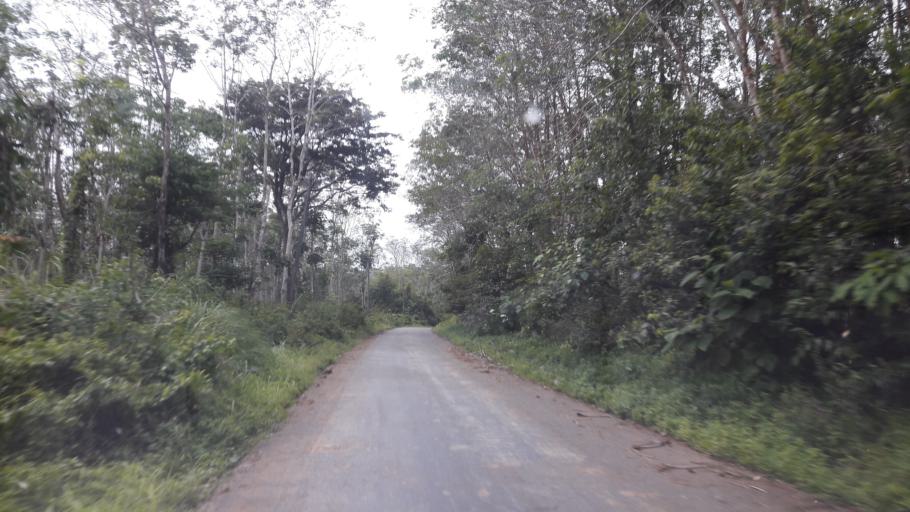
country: ID
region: South Sumatra
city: Gunungmenang
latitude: -3.1183
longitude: 104.1179
